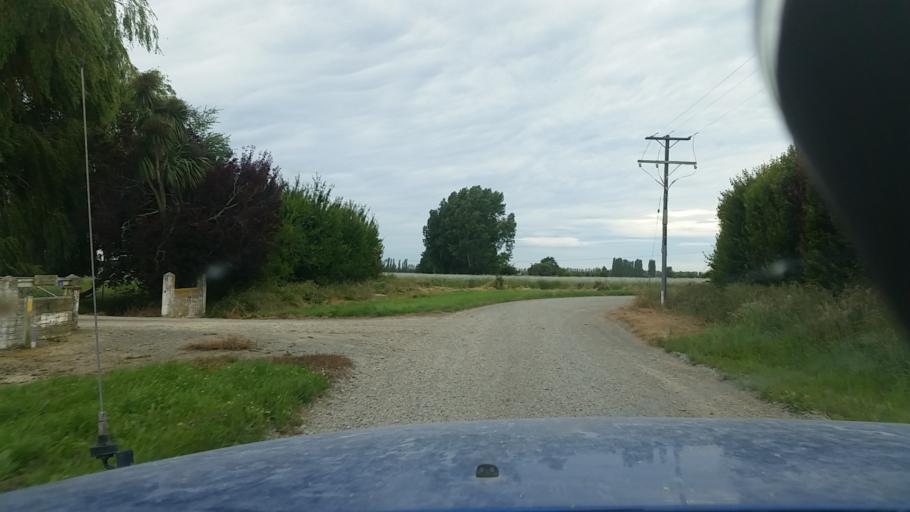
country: NZ
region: Canterbury
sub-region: Ashburton District
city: Ashburton
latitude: -43.8459
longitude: 171.6606
